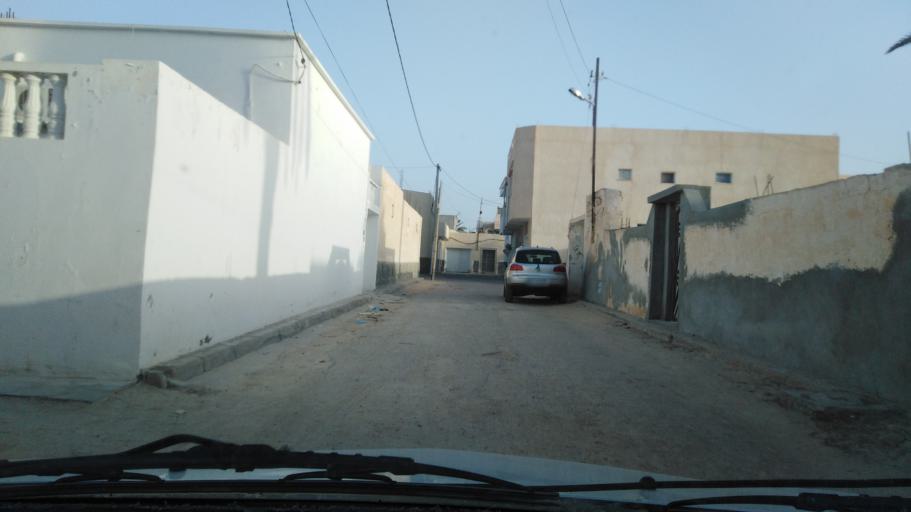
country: TN
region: Qabis
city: Gabes
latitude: 33.9584
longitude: 9.9969
